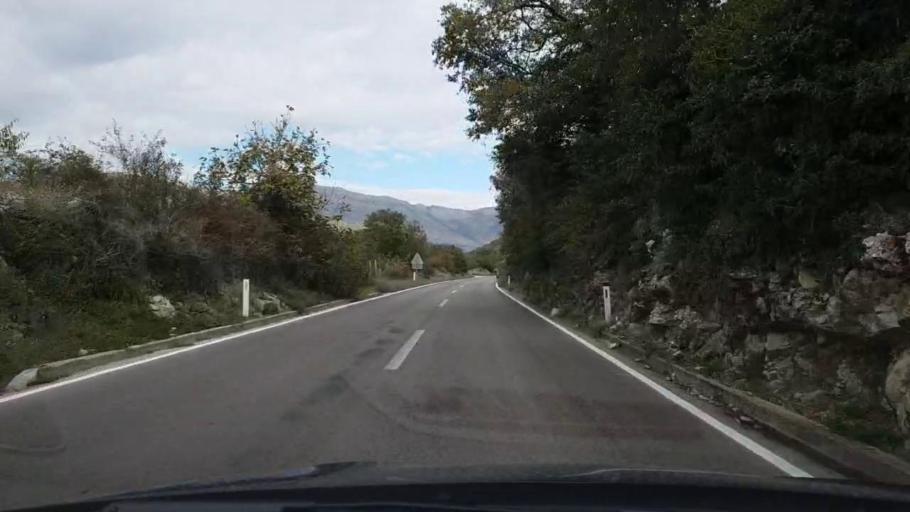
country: BA
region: Republika Srpska
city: Trebinje
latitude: 42.6825
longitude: 18.3028
